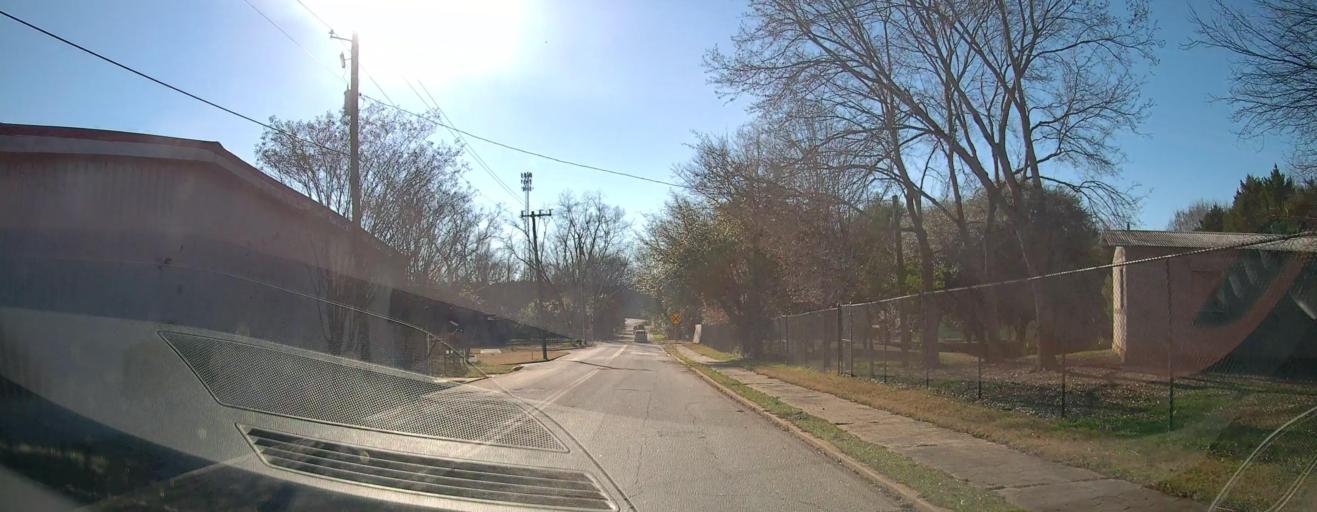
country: US
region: Georgia
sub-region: Sumter County
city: Americus
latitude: 32.0700
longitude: -84.2409
